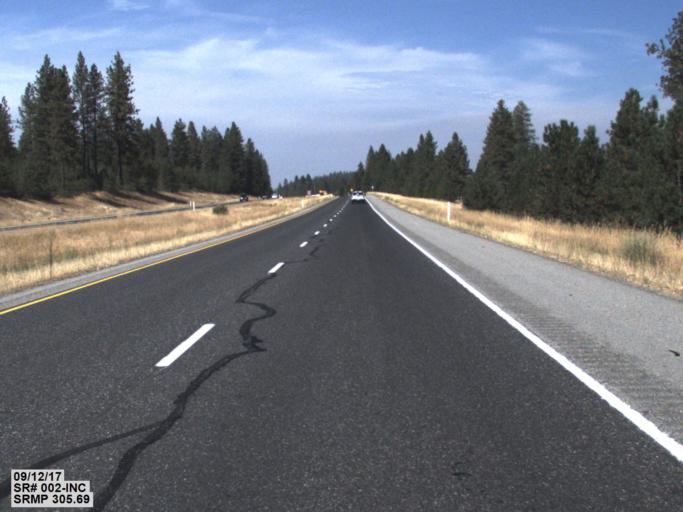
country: US
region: Washington
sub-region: Spokane County
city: Deer Park
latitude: 47.9067
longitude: -117.3506
